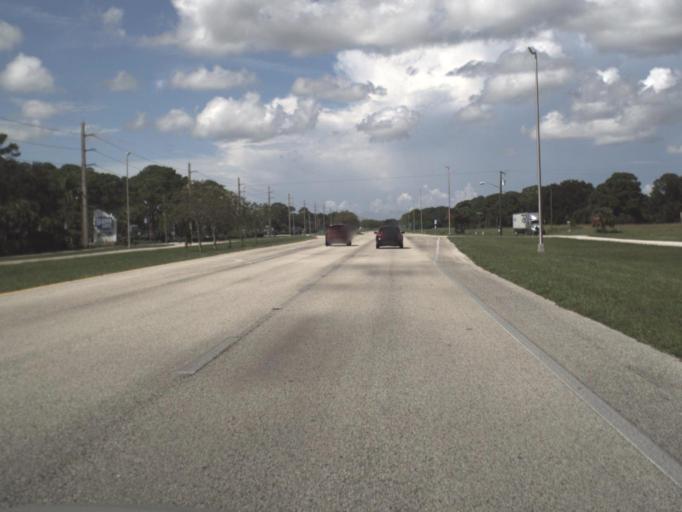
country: US
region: Florida
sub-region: Sarasota County
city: Warm Mineral Springs
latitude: 27.0475
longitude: -82.2678
